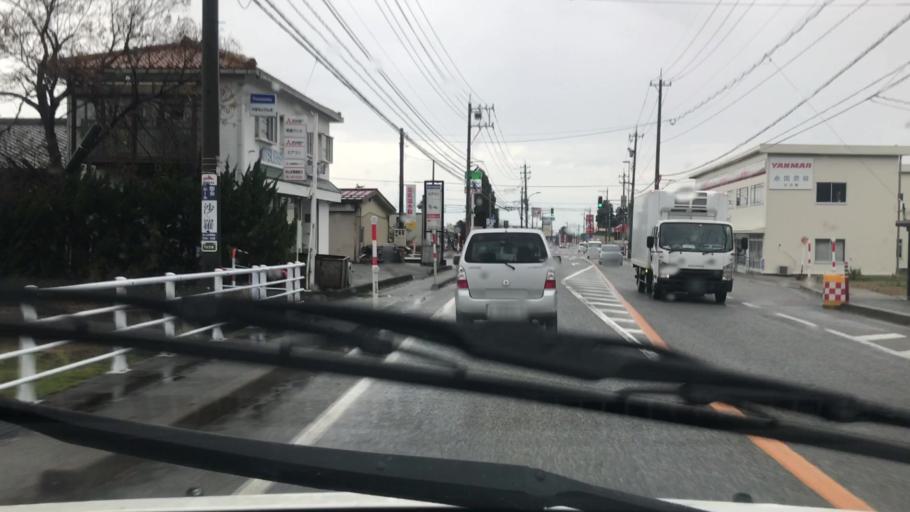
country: JP
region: Toyama
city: Yatsuomachi-higashikumisaka
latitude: 36.6039
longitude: 137.2033
